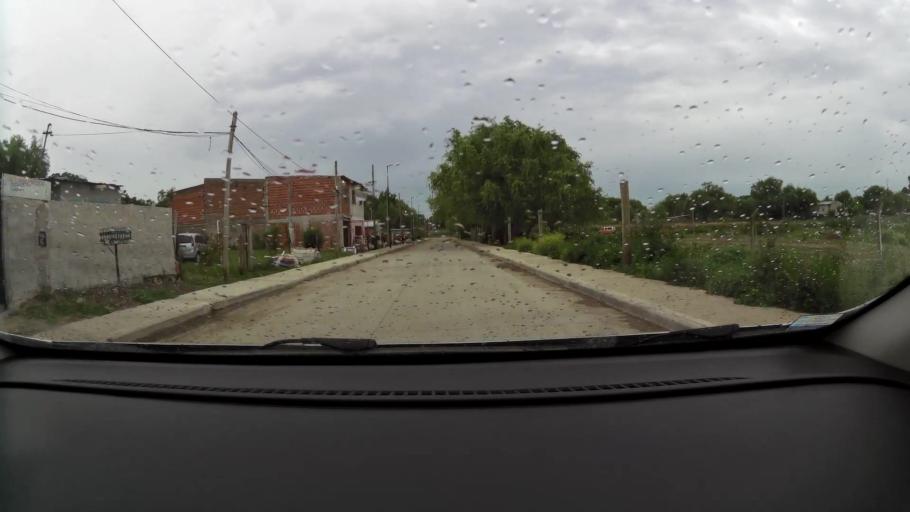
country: AR
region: Buenos Aires
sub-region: Partido de Zarate
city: Zarate
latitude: -34.1177
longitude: -59.0401
